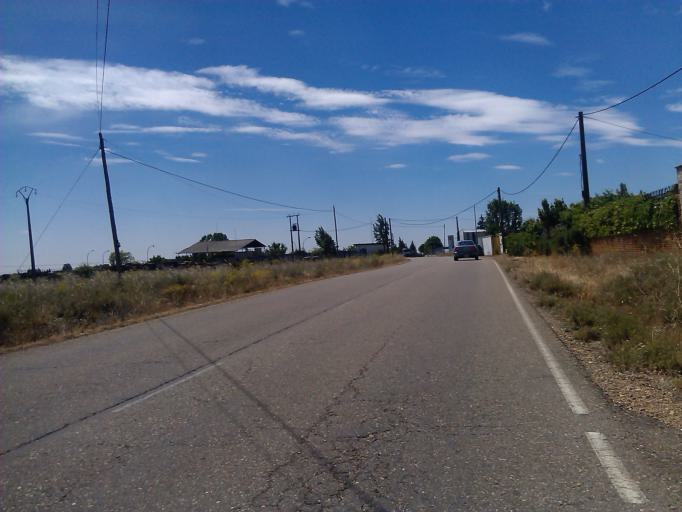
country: ES
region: Castille and Leon
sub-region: Provincia de Leon
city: Valverde de la Virgen
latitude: 42.5757
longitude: -5.6501
